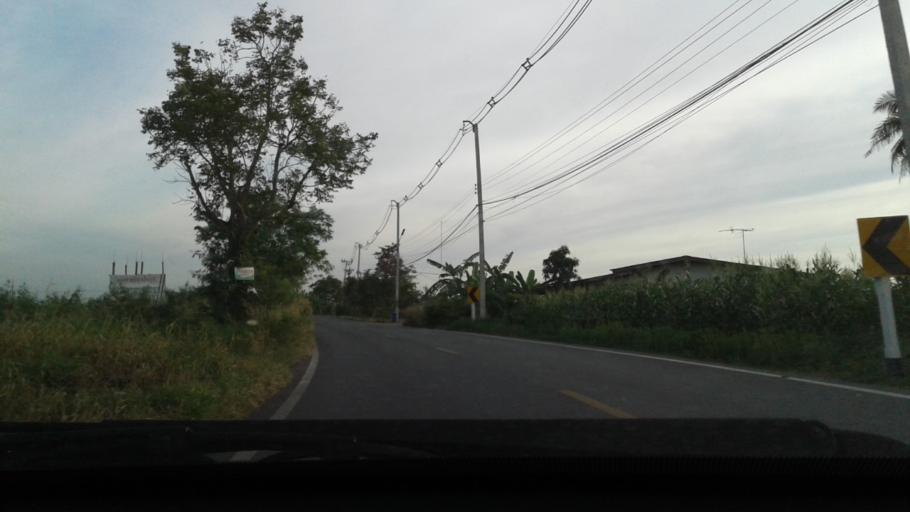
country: TH
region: Nonthaburi
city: Sai Noi
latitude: 13.9118
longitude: 100.2563
